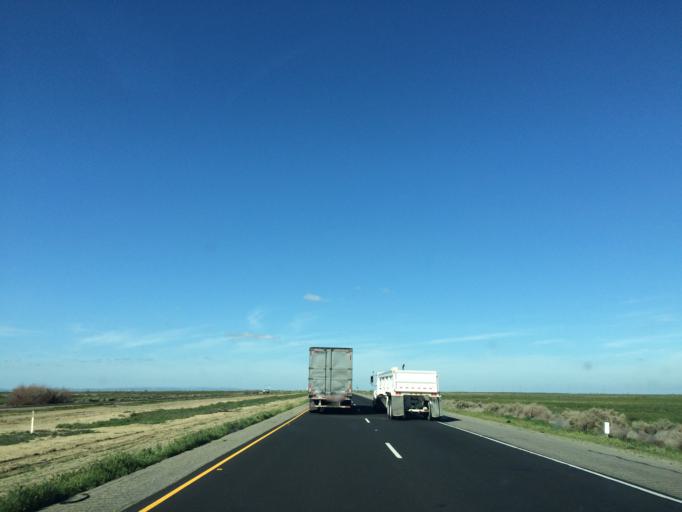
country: US
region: California
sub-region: Kern County
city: Lost Hills
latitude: 35.7622
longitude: -119.7617
